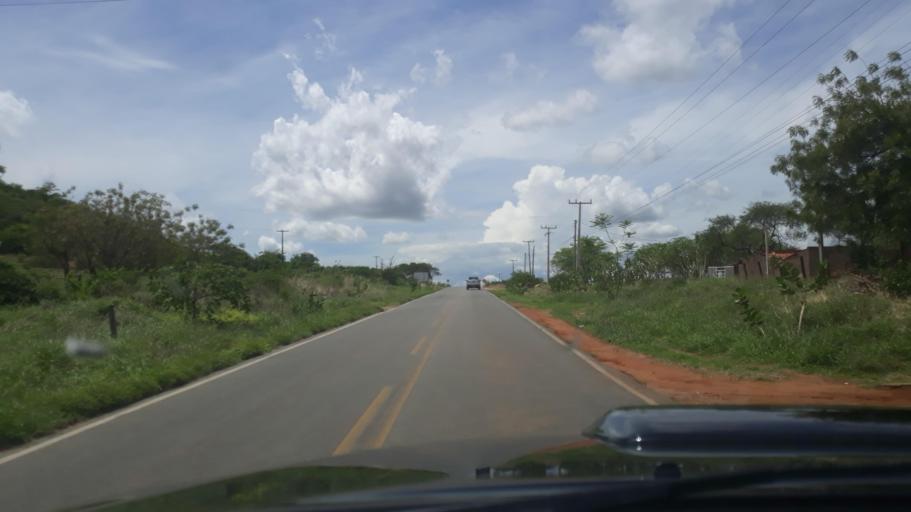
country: BR
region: Bahia
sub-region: Guanambi
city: Guanambi
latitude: -14.2629
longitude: -42.7212
